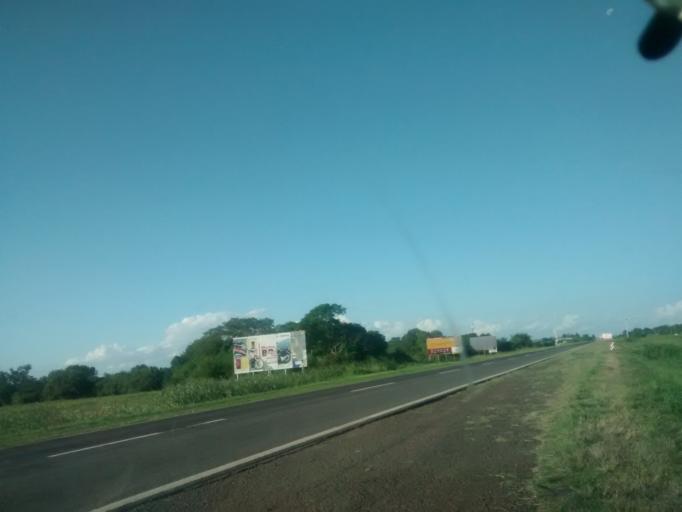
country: AR
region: Chaco
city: Fontana
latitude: -27.4812
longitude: -59.0626
